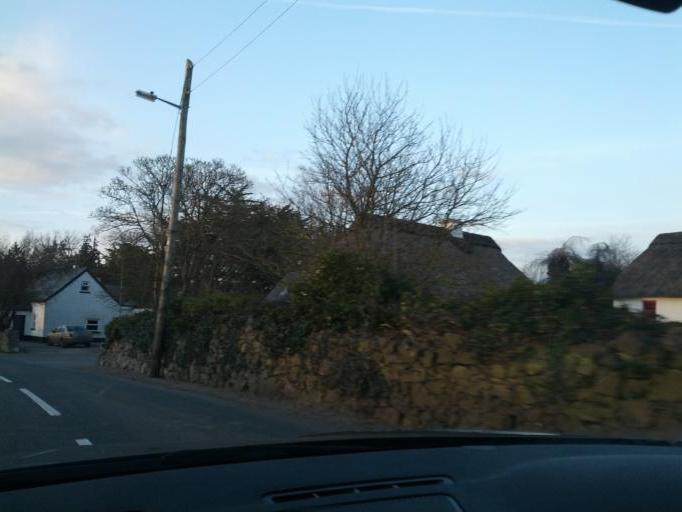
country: IE
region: Munster
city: Nenagh Bridge
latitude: 52.9327
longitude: -8.2385
